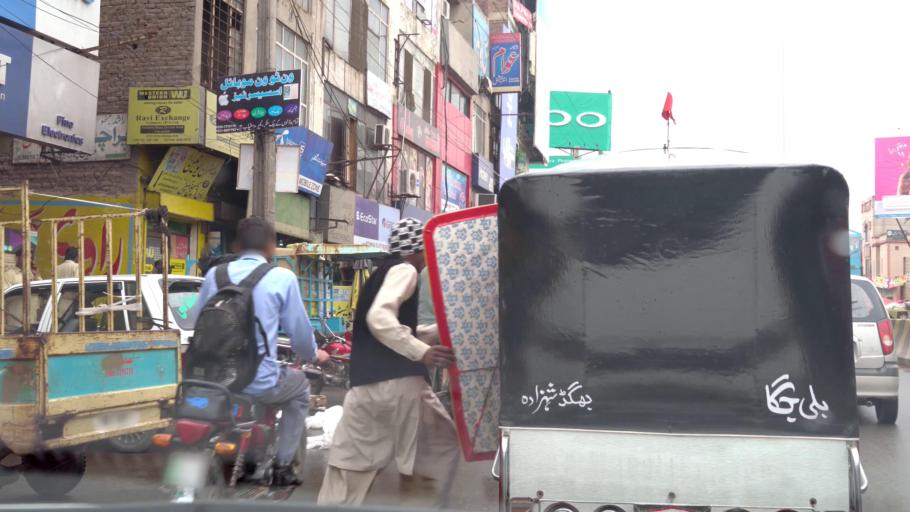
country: PK
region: Punjab
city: Faisalabad
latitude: 31.4179
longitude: 73.0857
